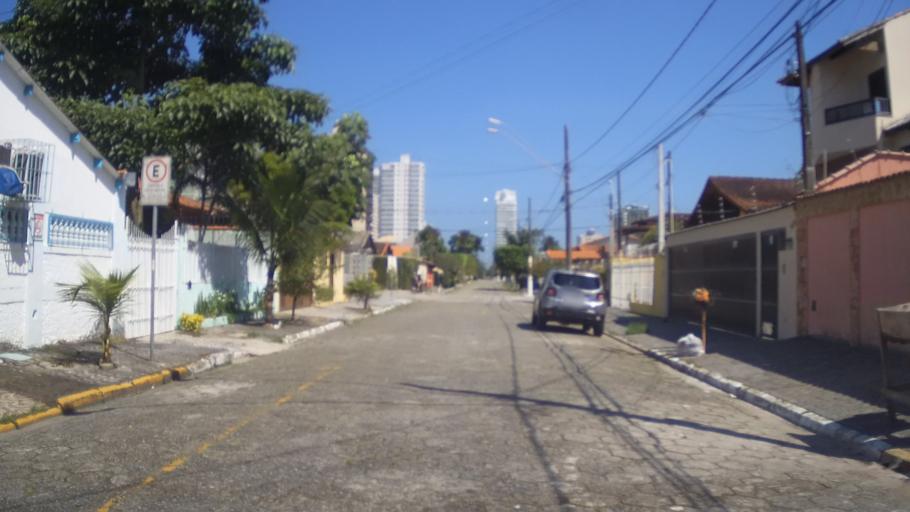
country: BR
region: Sao Paulo
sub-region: Praia Grande
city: Praia Grande
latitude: -24.0082
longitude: -46.4026
